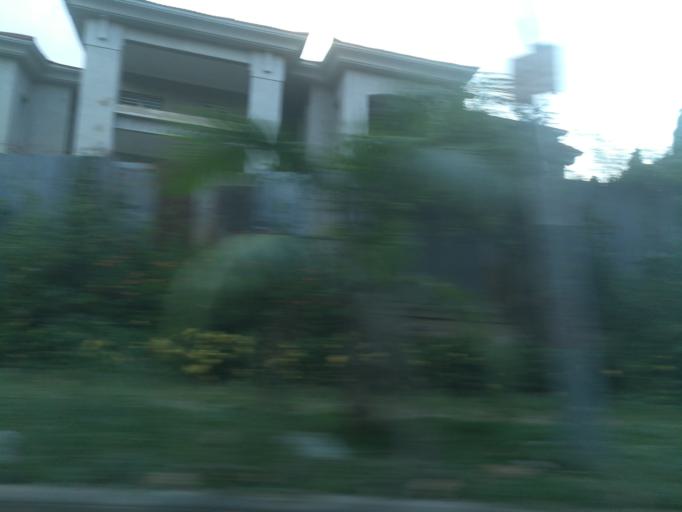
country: NG
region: Abuja Federal Capital Territory
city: Abuja
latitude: 9.0721
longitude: 7.4112
